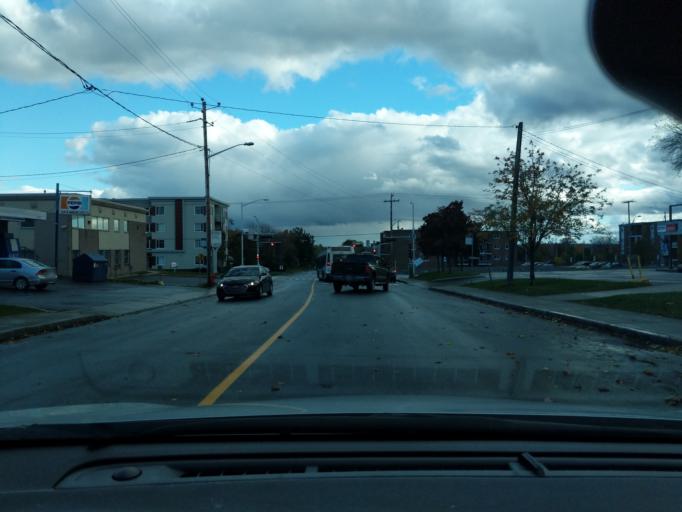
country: CA
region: Quebec
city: L'Ancienne-Lorette
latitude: 46.7632
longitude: -71.2831
